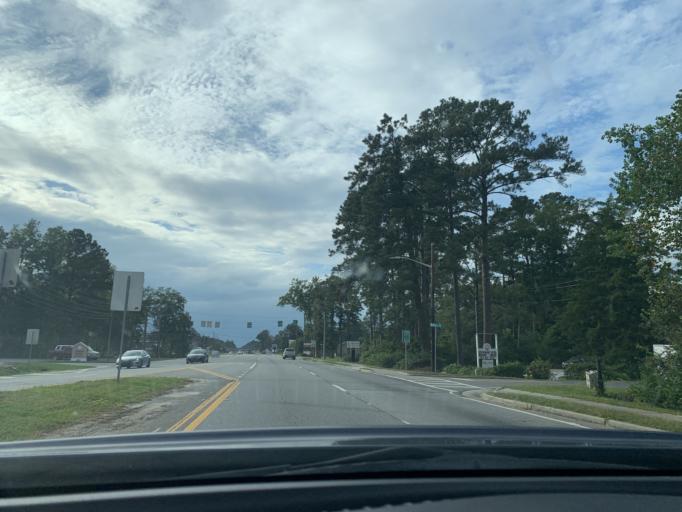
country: US
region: Georgia
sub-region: Chatham County
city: Pooler
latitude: 32.1190
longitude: -81.2570
